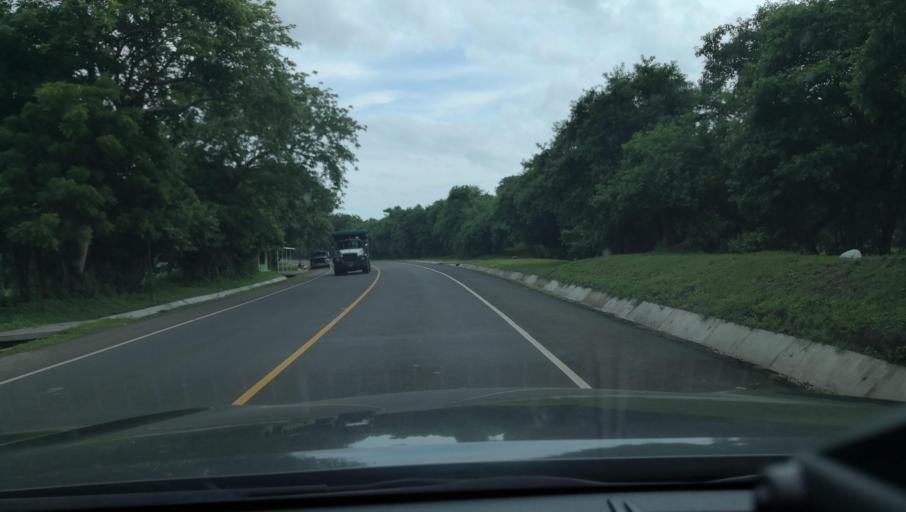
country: NI
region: Masaya
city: Nindiri
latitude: 12.0734
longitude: -86.1382
